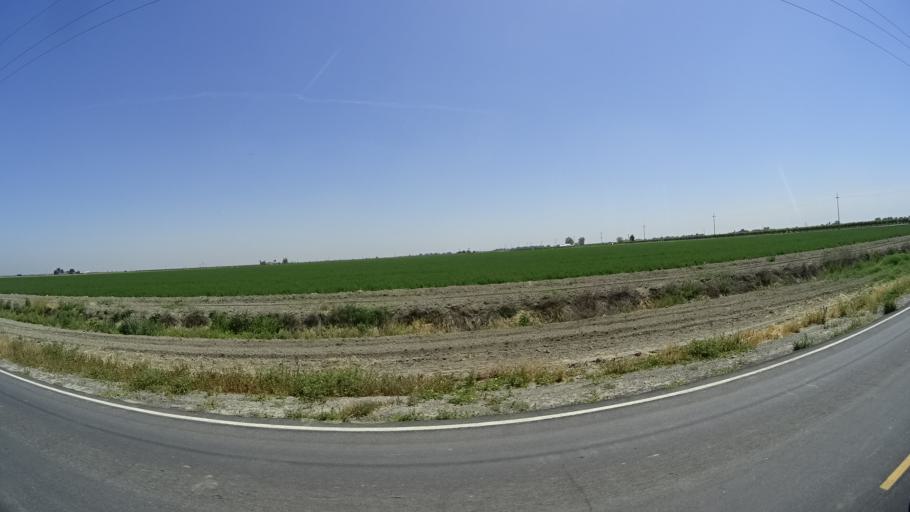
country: US
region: California
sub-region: Kings County
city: Corcoran
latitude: 36.0524
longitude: -119.5363
